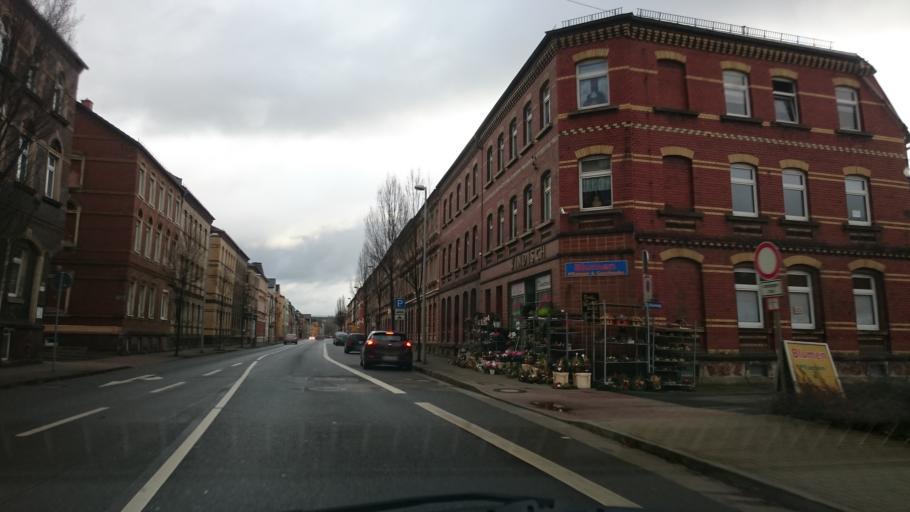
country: DE
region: Saxony
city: Wilkau-Hasslau
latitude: 50.6783
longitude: 12.5096
